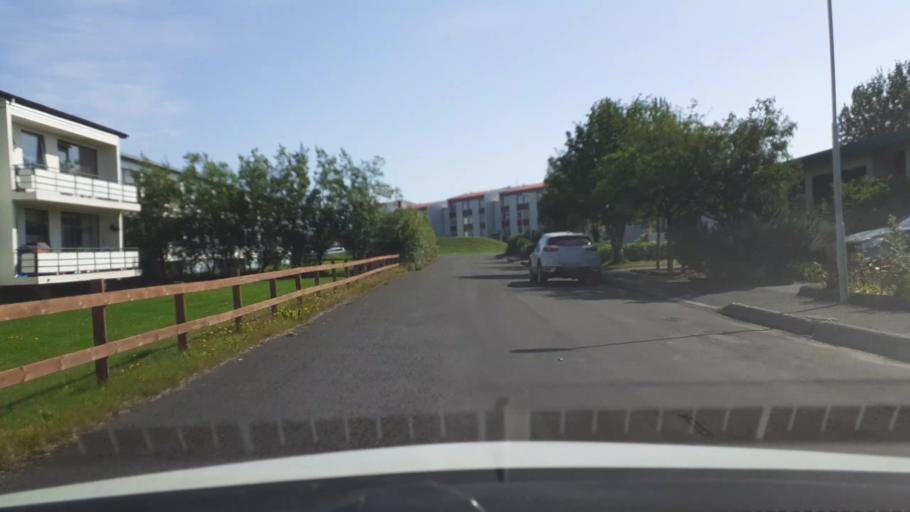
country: IS
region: South
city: Selfoss
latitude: 63.9315
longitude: -21.0032
